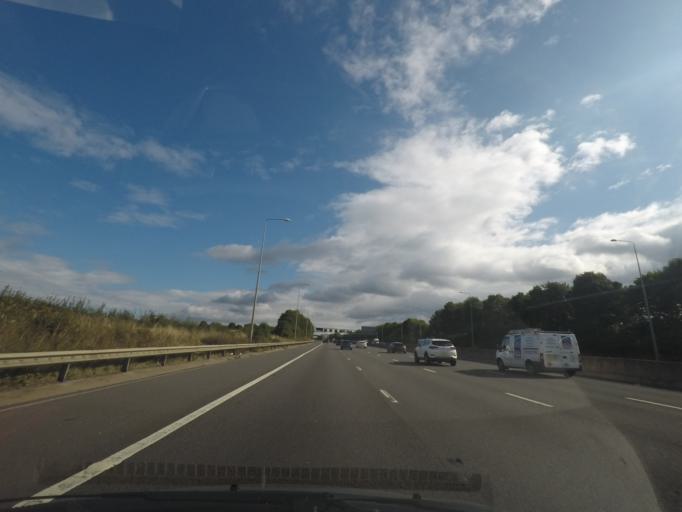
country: GB
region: England
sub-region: Derbyshire
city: Pinxton
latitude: 53.0855
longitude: -1.3003
